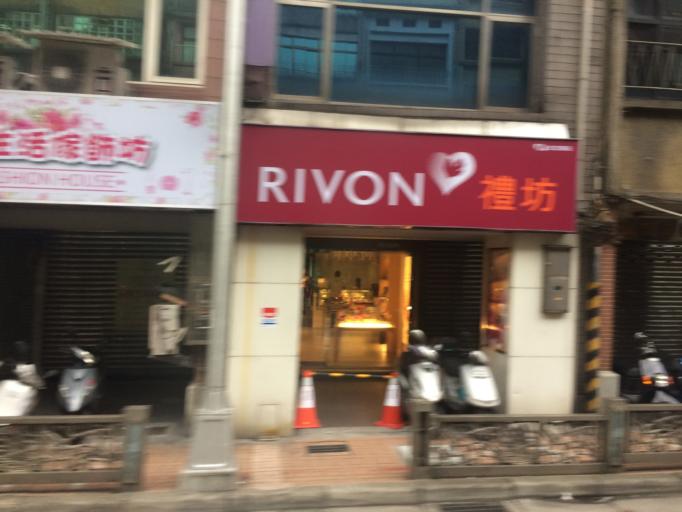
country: TW
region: Taiwan
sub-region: Keelung
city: Keelung
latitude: 25.1296
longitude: 121.7402
